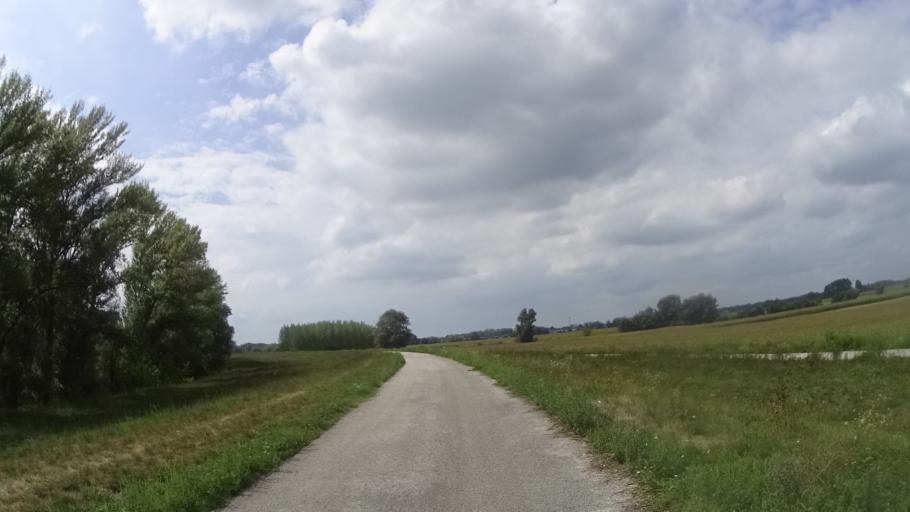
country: SK
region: Trnavsky
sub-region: Okres Dunajska Streda
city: Velky Meder
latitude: 47.7953
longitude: 17.6810
